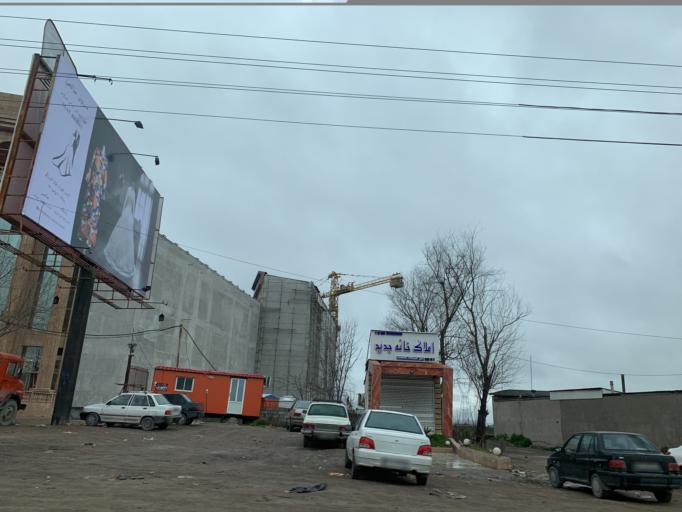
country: IR
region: Mazandaran
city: Amol
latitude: 36.4127
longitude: 52.3483
